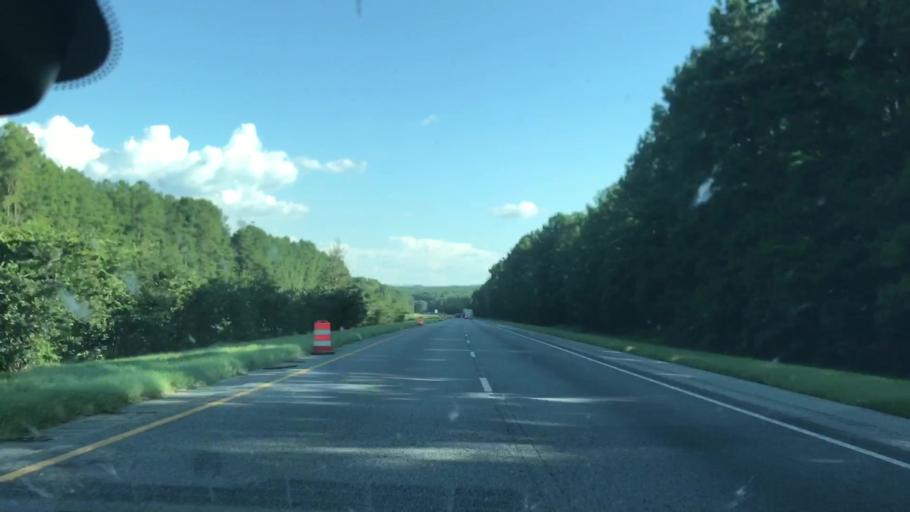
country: US
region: Georgia
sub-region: Harris County
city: Hamilton
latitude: 32.6486
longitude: -84.9721
